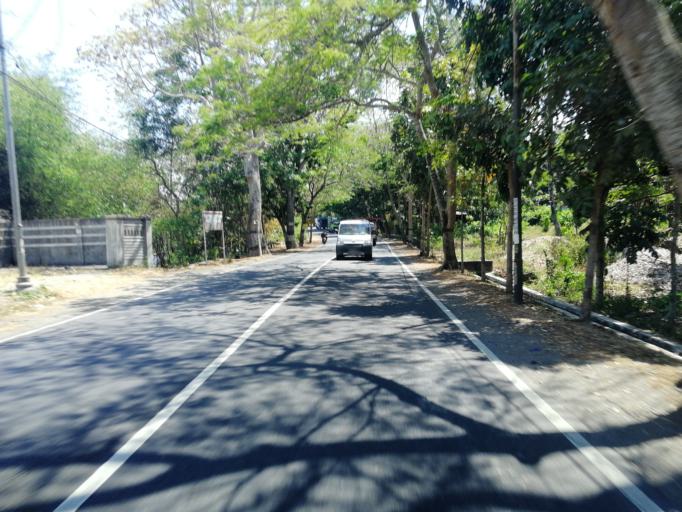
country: ID
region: West Nusa Tenggara
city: Jelateng Timur
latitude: -8.6947
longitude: 116.1080
